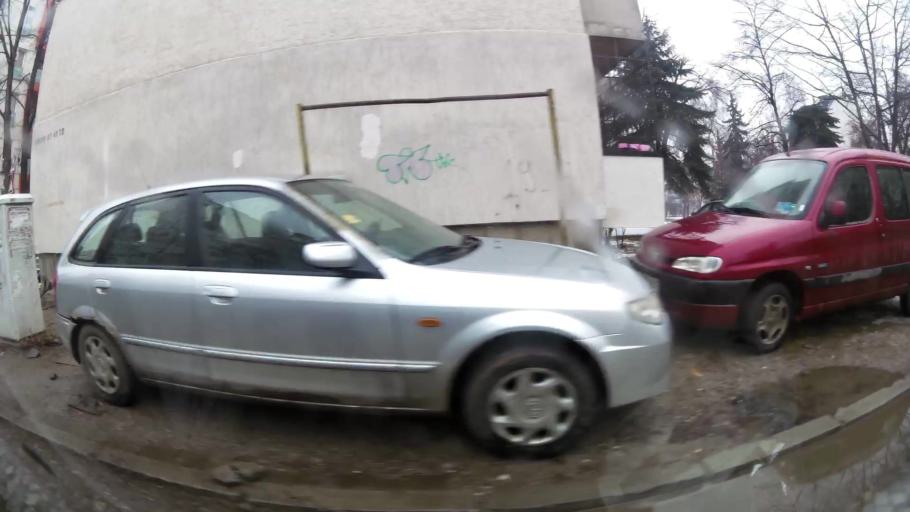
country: BG
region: Sofia-Capital
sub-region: Stolichna Obshtina
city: Sofia
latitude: 42.6685
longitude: 23.2715
